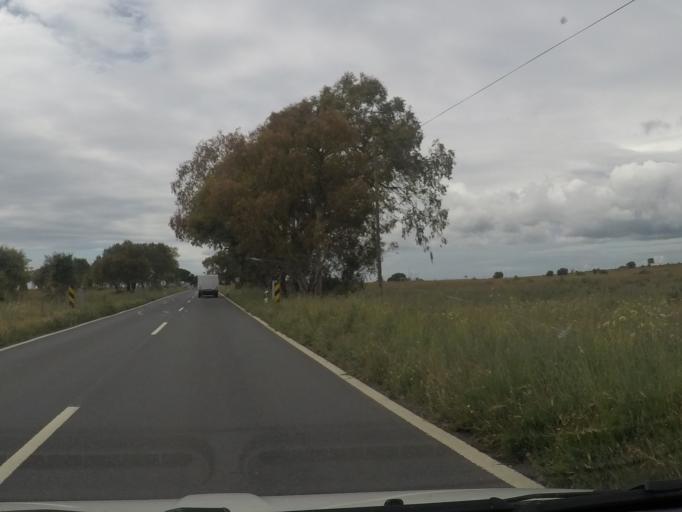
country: PT
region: Setubal
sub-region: Sines
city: Porto Covo
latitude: 37.8859
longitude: -8.7534
